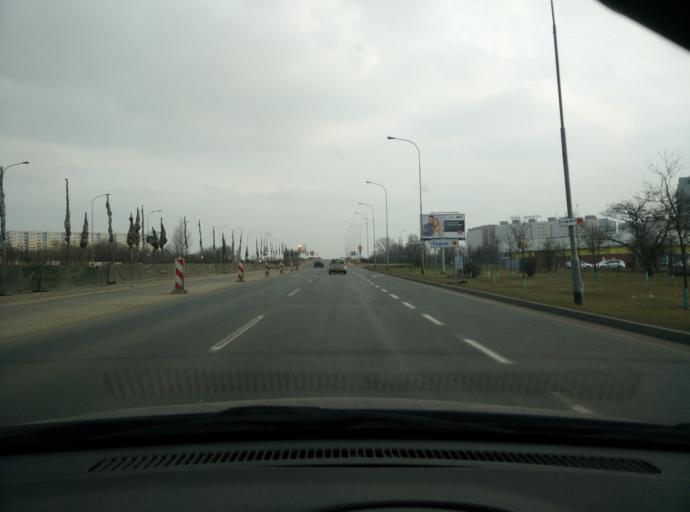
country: PL
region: Greater Poland Voivodeship
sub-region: Poznan
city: Poznan
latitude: 52.3872
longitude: 16.9686
